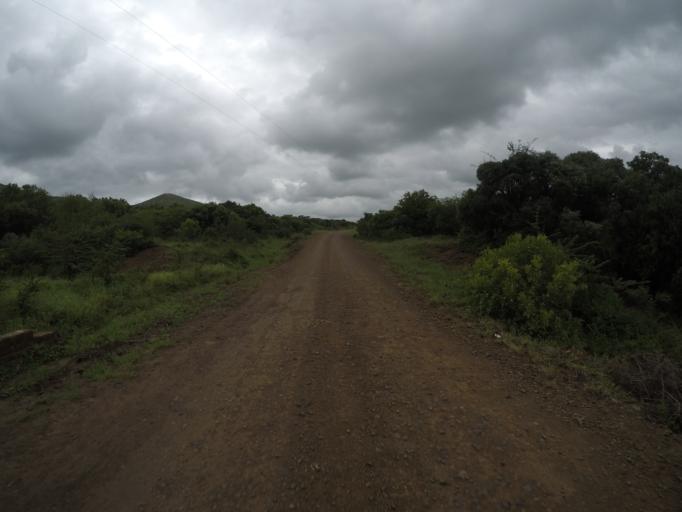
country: ZA
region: KwaZulu-Natal
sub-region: uThungulu District Municipality
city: Empangeni
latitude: -28.5697
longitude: 31.8736
